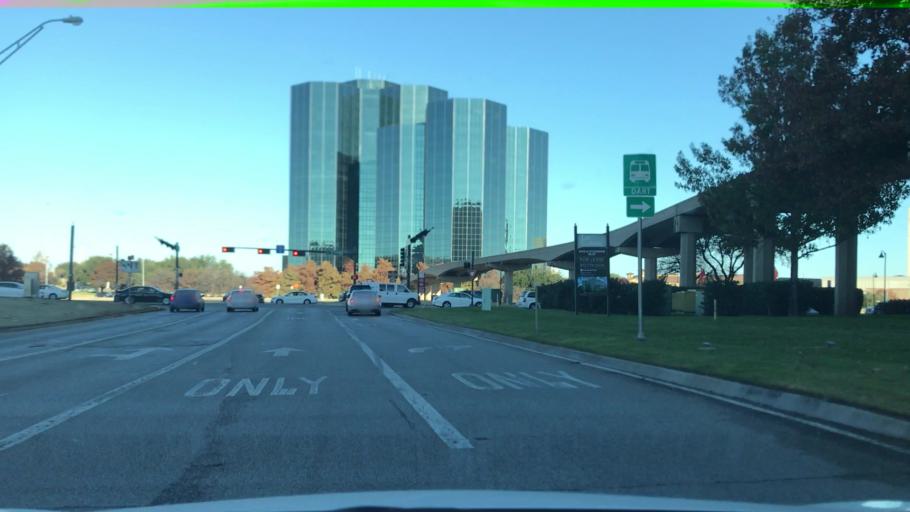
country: US
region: Texas
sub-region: Dallas County
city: Irving
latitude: 32.8684
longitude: -96.9419
